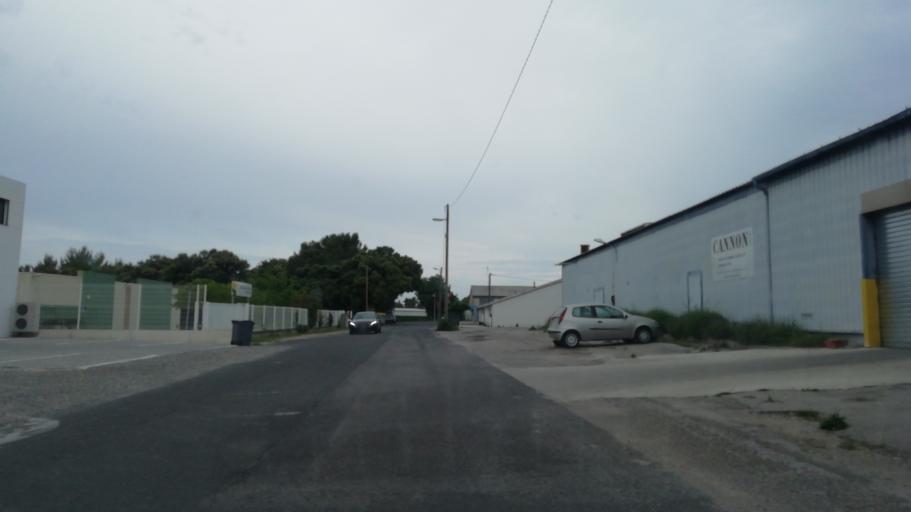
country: FR
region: Languedoc-Roussillon
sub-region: Departement de l'Herault
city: Saint-Mathieu-de-Treviers
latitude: 43.7638
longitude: 3.8724
